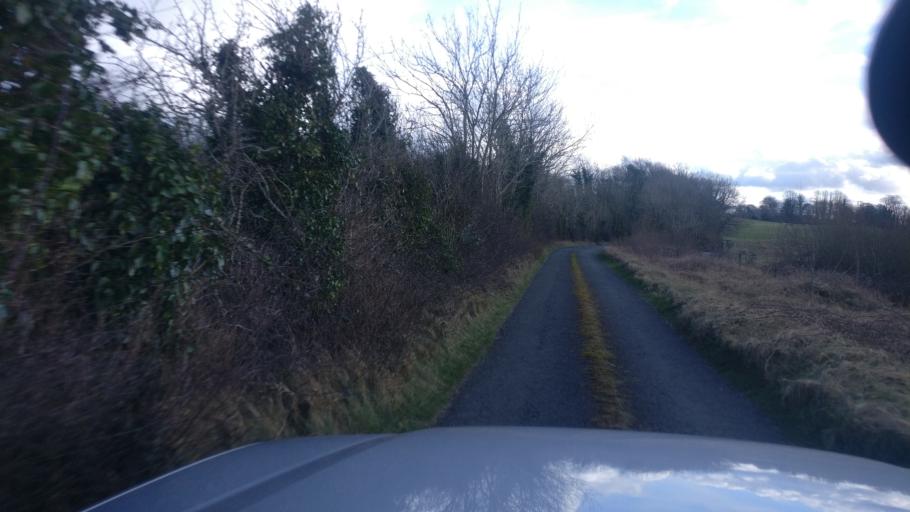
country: IE
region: Connaught
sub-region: County Galway
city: Loughrea
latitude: 53.1876
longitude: -8.4284
